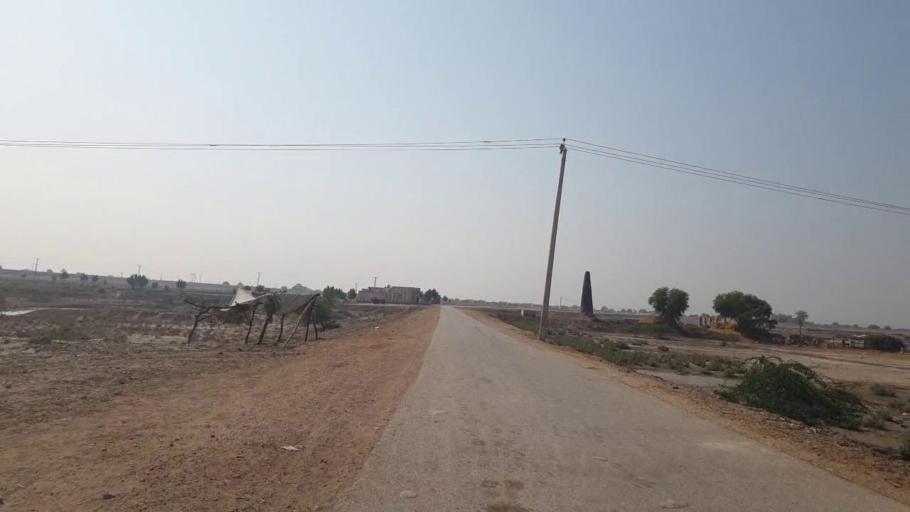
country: PK
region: Sindh
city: Sehwan
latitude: 26.4344
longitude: 67.8449
